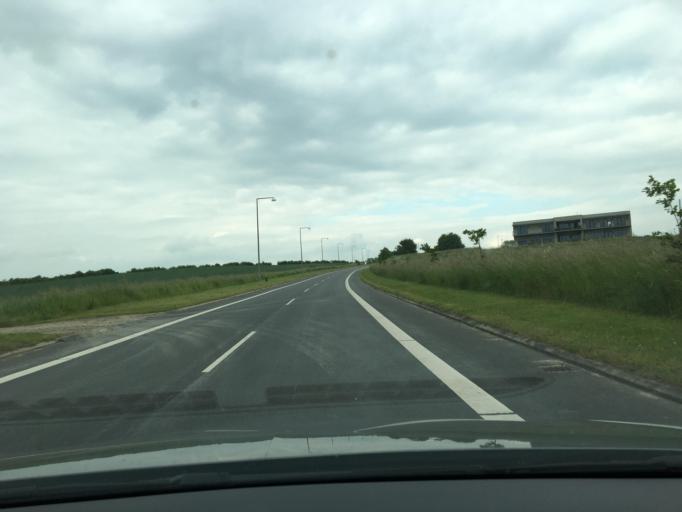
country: DK
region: South Denmark
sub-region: Assens Kommune
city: Assens
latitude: 55.2767
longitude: 9.9022
